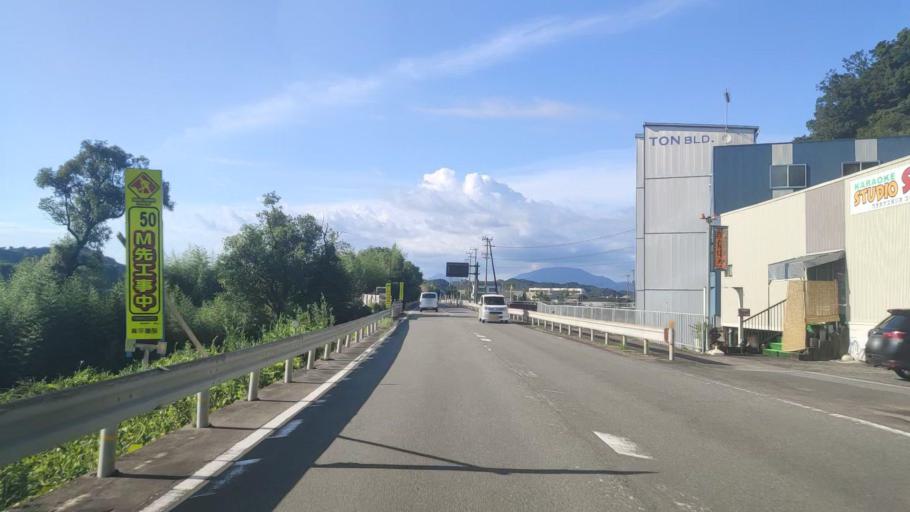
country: JP
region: Wakayama
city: Tanabe
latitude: 33.6691
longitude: 135.4082
